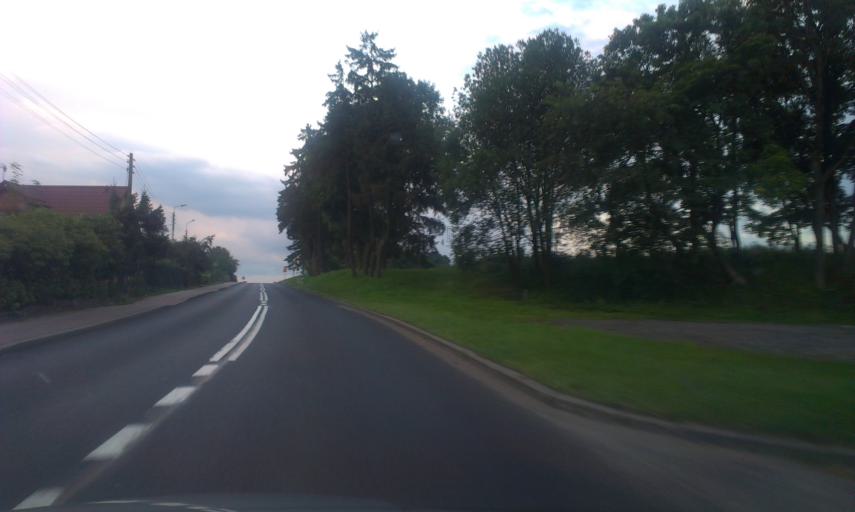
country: PL
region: West Pomeranian Voivodeship
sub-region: Powiat koszalinski
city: Bobolice
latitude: 54.0287
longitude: 16.4637
